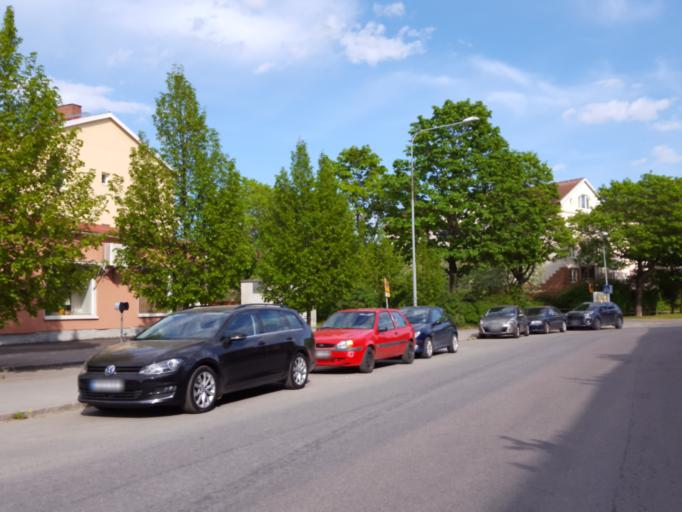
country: SE
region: Uppsala
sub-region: Uppsala Kommun
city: Uppsala
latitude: 59.8674
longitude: 17.6647
